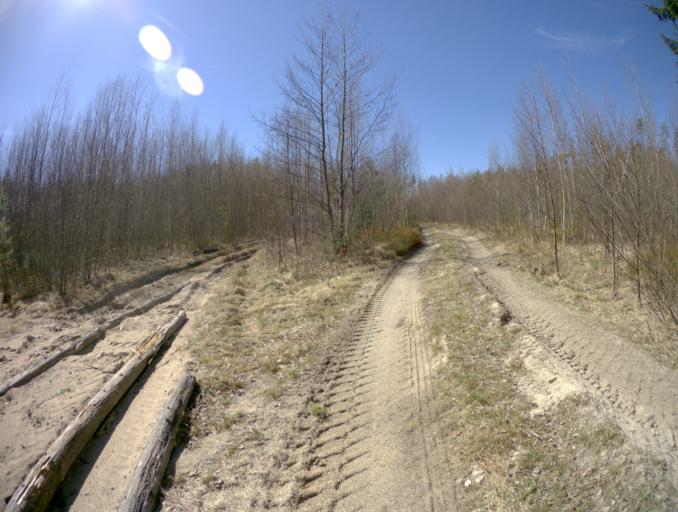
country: RU
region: Vladimir
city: Ivanishchi
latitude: 55.8367
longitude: 40.4547
